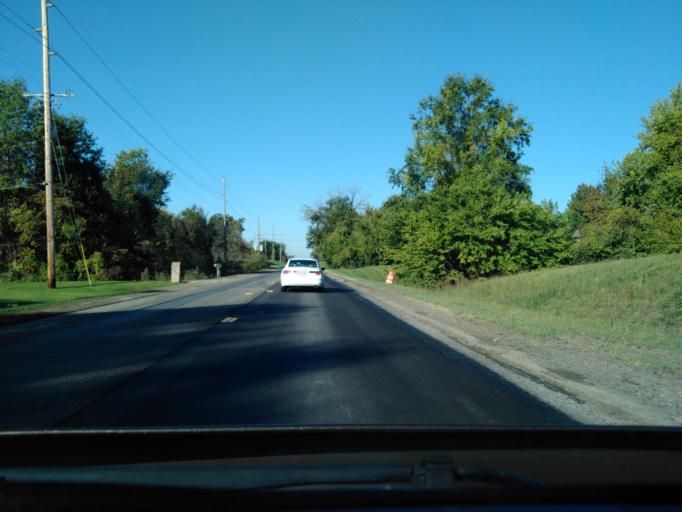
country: US
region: Illinois
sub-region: Madison County
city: Troy
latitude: 38.7177
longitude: -89.8599
